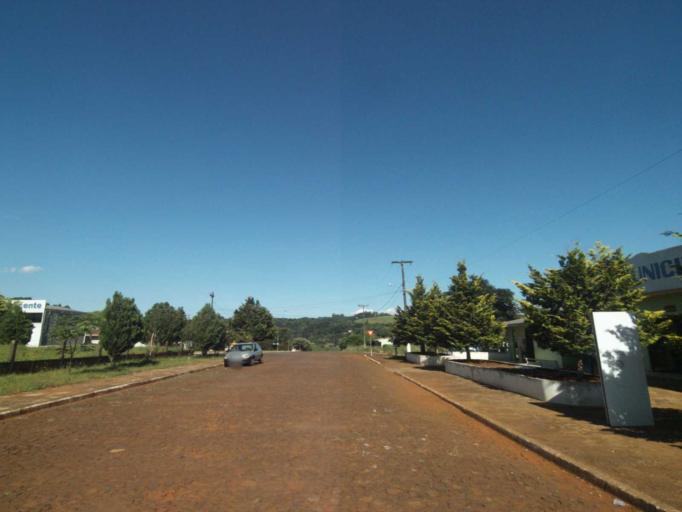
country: BR
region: Parana
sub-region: Laranjeiras Do Sul
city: Laranjeiras do Sul
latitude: -25.3826
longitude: -52.2002
